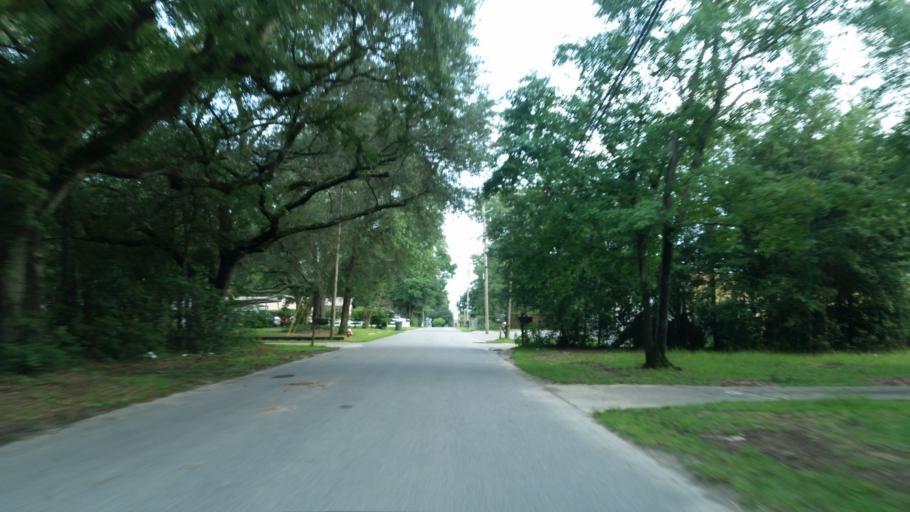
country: US
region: Florida
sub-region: Escambia County
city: Ferry Pass
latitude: 30.5127
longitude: -87.2064
